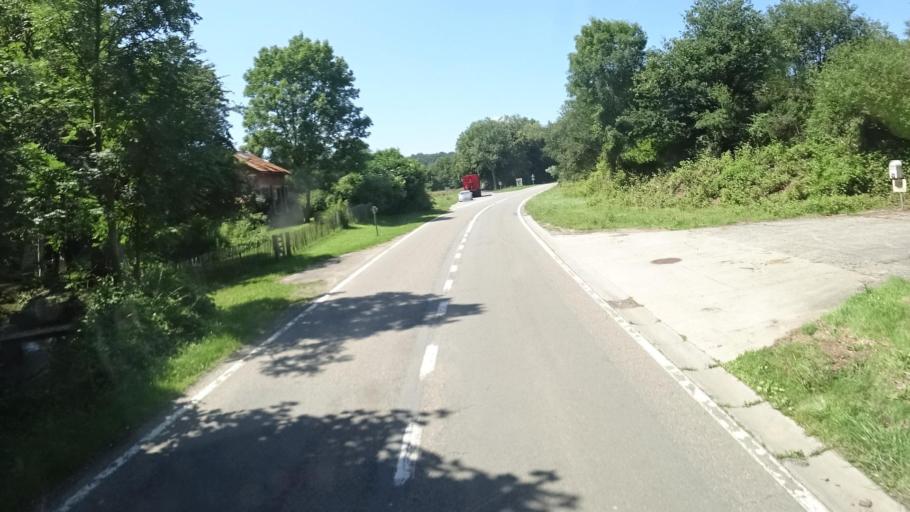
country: BE
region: Wallonia
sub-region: Province de Namur
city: Anhee
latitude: 50.3172
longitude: 4.8494
